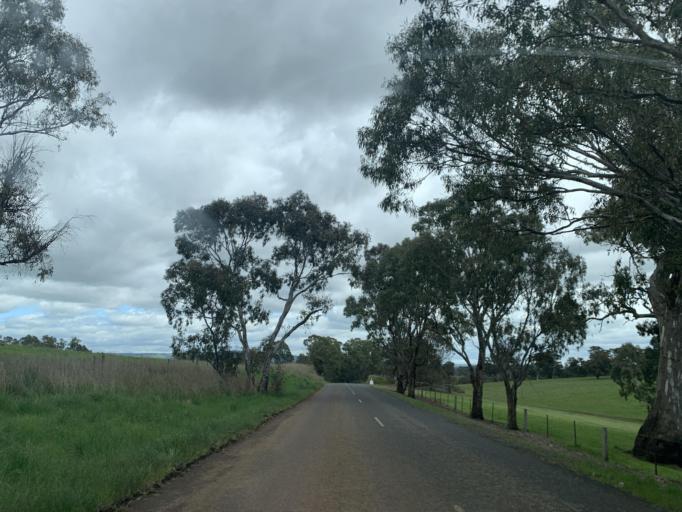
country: AU
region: Victoria
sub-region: Whittlesea
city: Whittlesea
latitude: -37.1859
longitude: 145.0197
